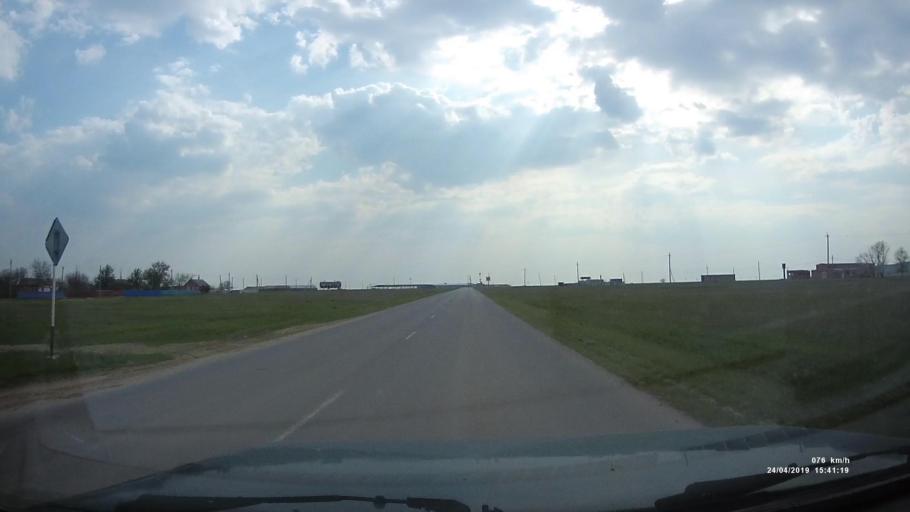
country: RU
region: Kalmykiya
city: Yashalta
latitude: 46.5723
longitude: 42.7981
